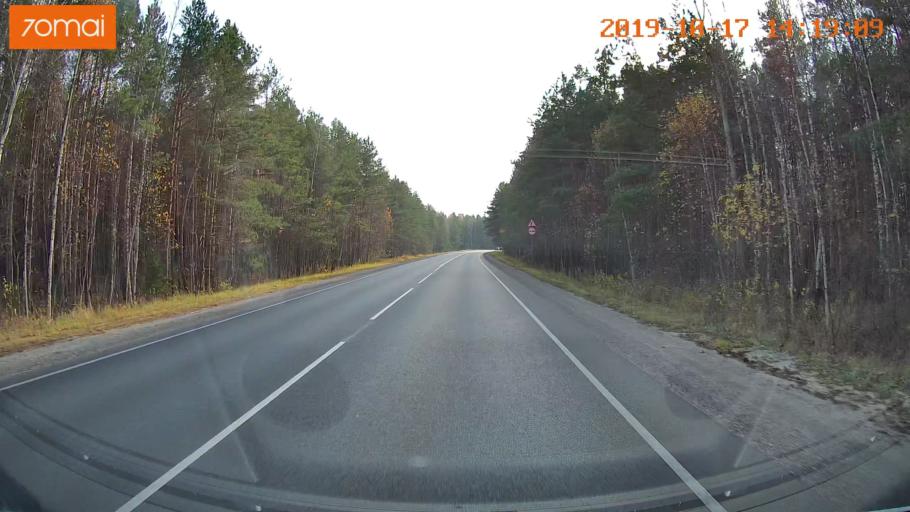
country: RU
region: Rjazan
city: Spas-Klepiki
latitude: 55.0536
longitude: 40.0238
